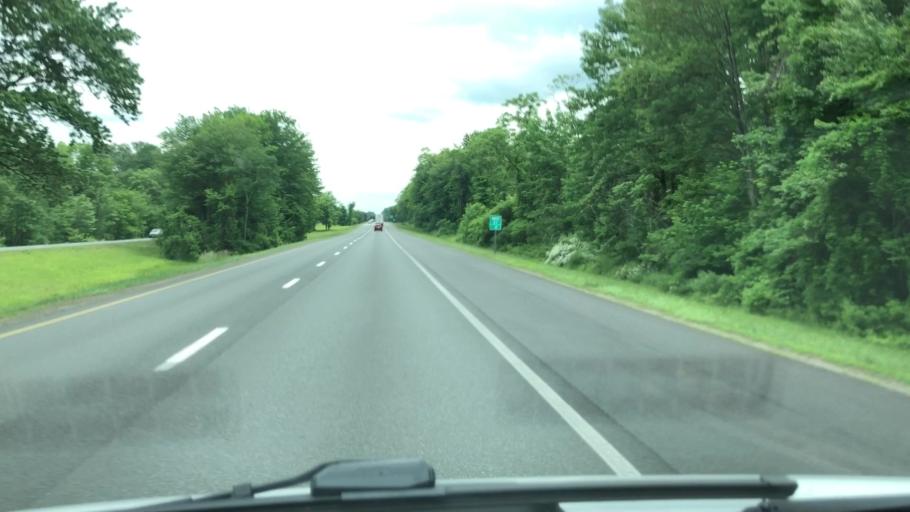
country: US
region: Massachusetts
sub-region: Franklin County
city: Whately
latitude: 42.4197
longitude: -72.6247
